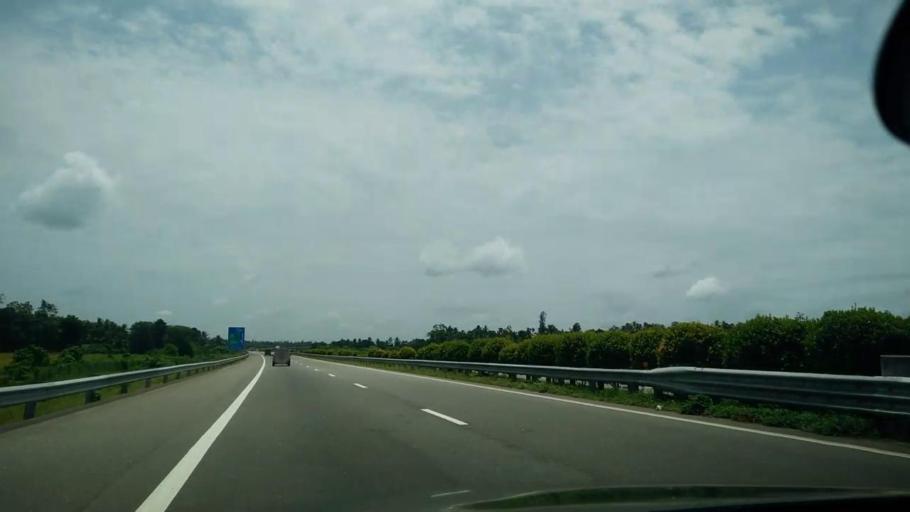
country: LK
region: Western
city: Homagama
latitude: 6.8740
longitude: 79.9779
